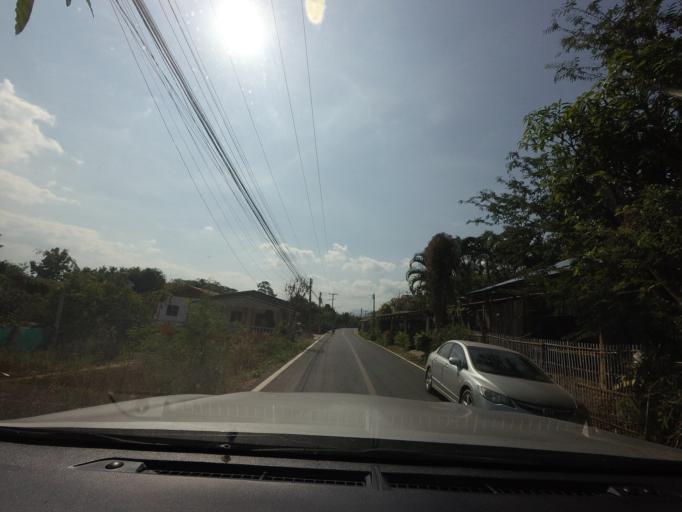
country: TH
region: Mae Hong Son
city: Wiang Nuea
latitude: 19.3850
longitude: 98.4394
